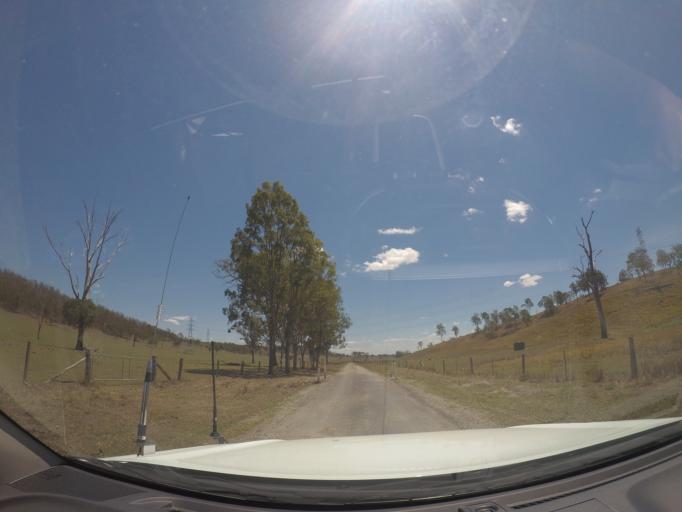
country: AU
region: Queensland
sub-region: Ipswich
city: Redbank Plains
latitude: -27.7520
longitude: 152.8334
